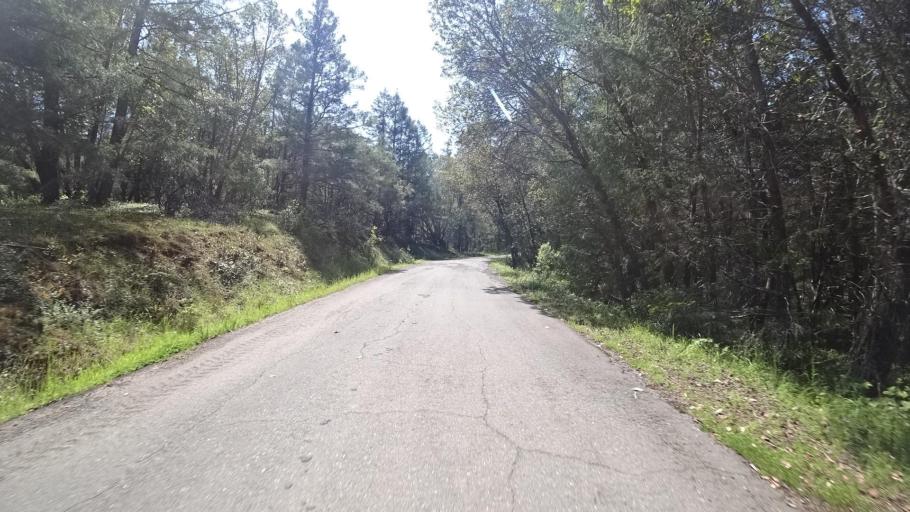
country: US
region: California
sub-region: Humboldt County
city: Redway
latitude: 40.2165
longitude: -123.6491
